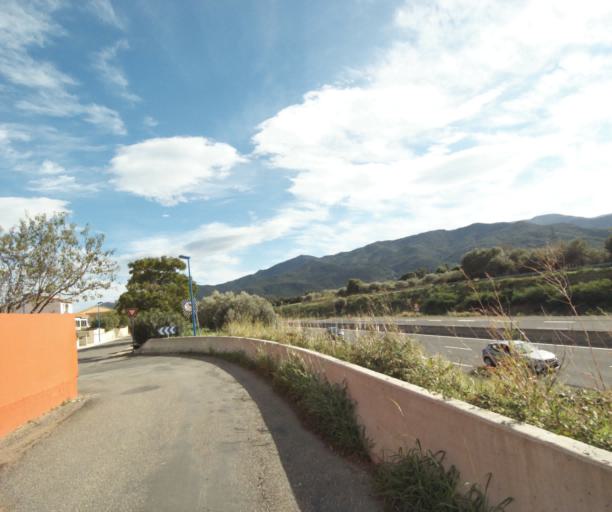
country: FR
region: Languedoc-Roussillon
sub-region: Departement des Pyrenees-Orientales
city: Argelers
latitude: 42.5463
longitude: 3.0080
